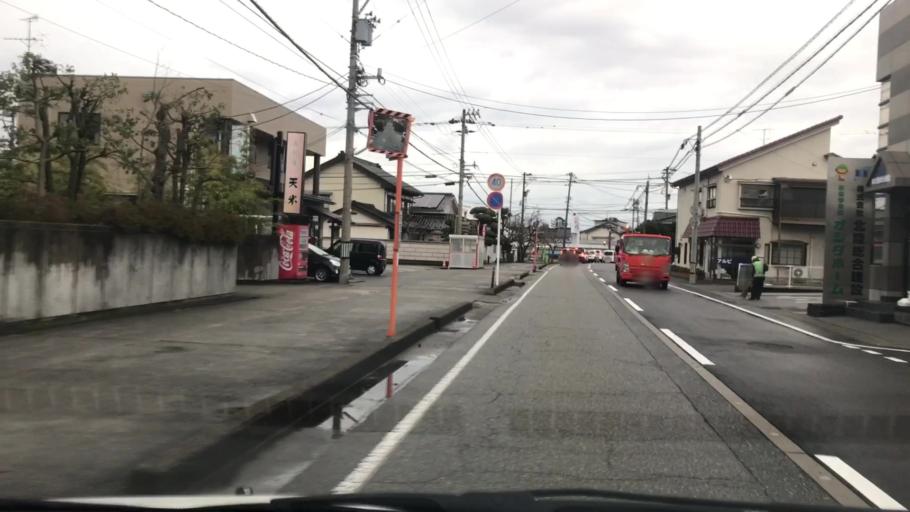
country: JP
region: Toyama
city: Toyama-shi
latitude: 36.6658
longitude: 137.2118
